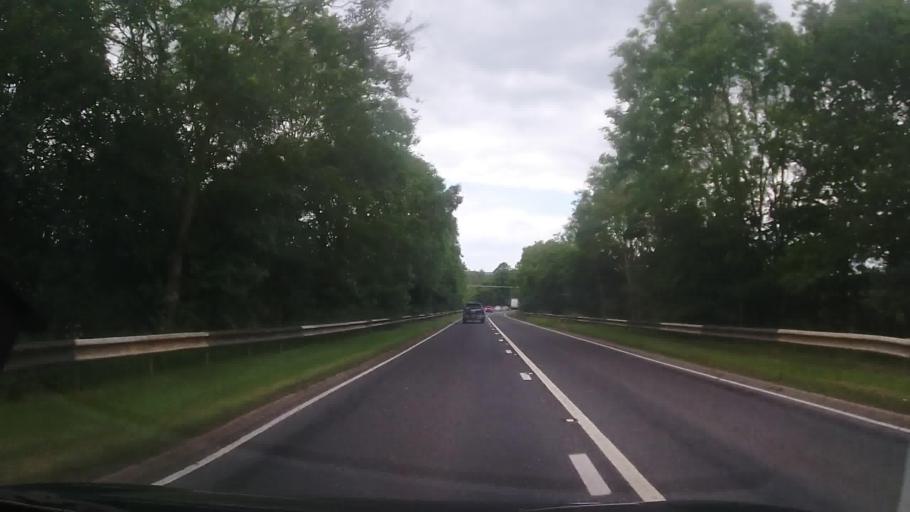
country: GB
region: England
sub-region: Herefordshire
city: Wellington
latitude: 52.0973
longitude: -2.7295
